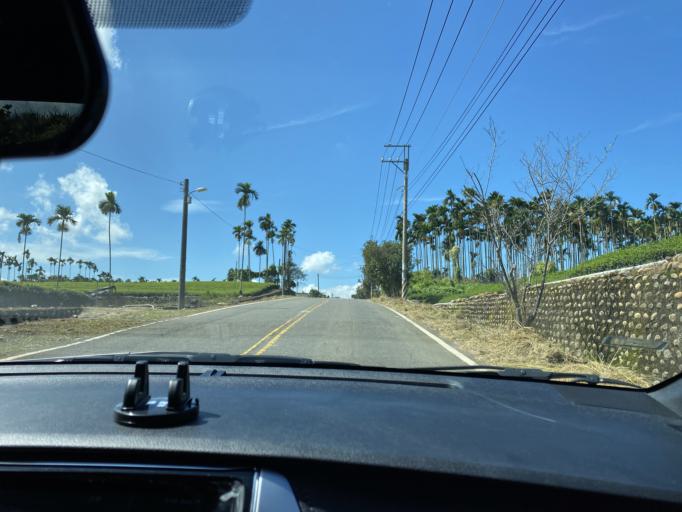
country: TW
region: Taiwan
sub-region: Nantou
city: Nantou
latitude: 23.8641
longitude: 120.6331
